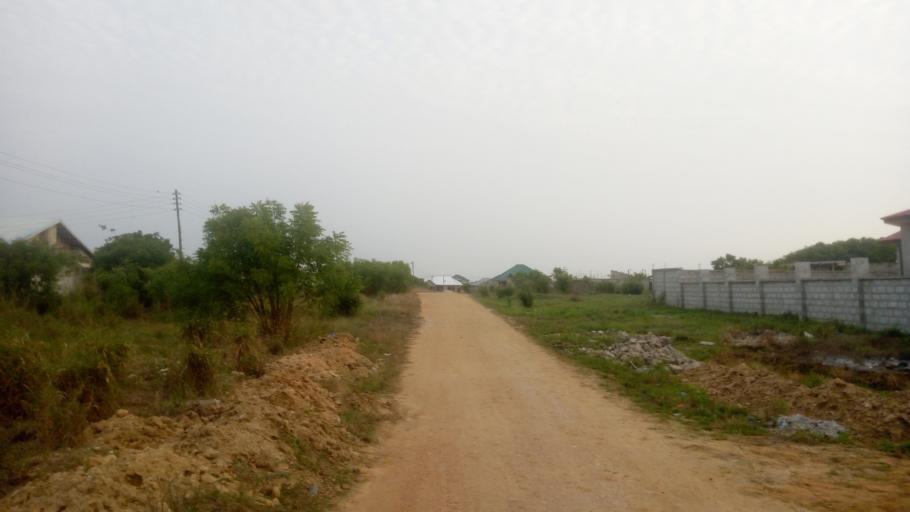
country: GH
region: Central
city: Winneba
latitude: 5.3806
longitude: -0.6287
